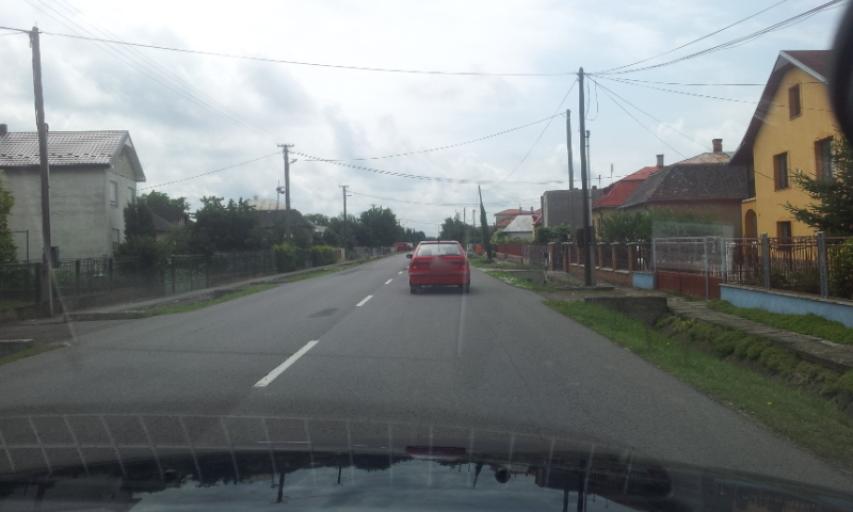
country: SK
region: Kosicky
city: Michalovce
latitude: 48.7004
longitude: 21.9708
